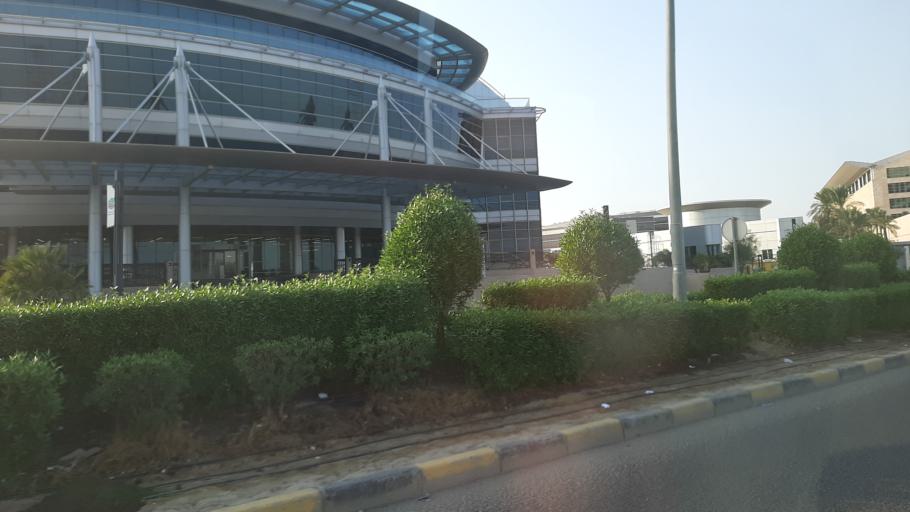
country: KW
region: Al Ahmadi
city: Al Ahmadi
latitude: 29.0906
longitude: 48.0881
